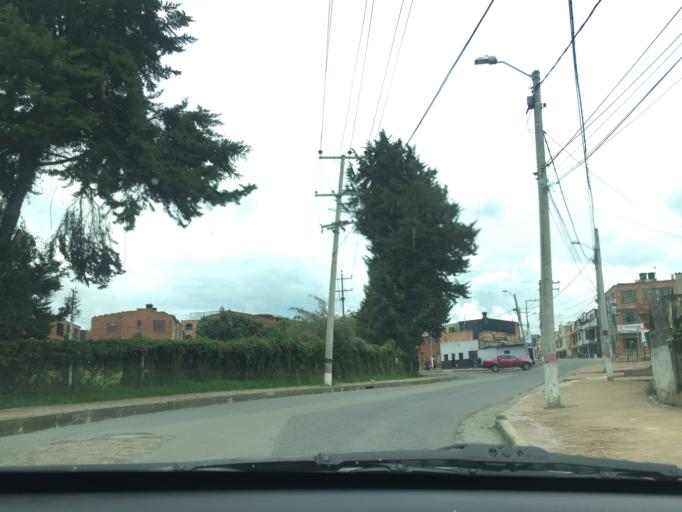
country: CO
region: Cundinamarca
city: El Rosal
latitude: 4.8491
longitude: -74.2604
